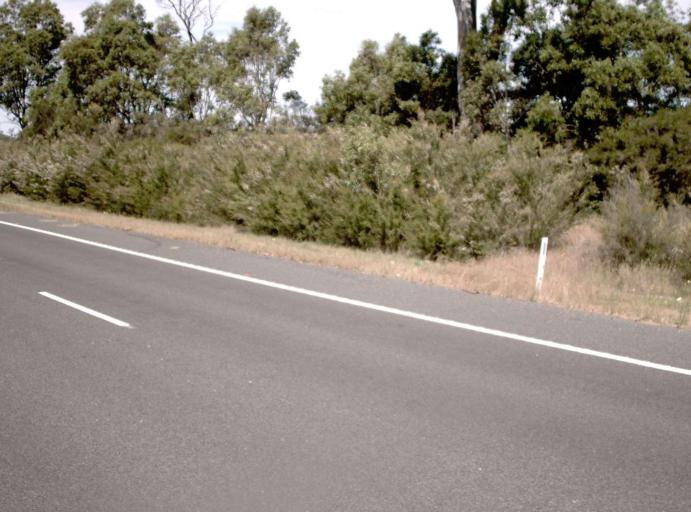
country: AU
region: Victoria
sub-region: Wellington
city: Sale
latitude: -37.9382
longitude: 147.1529
